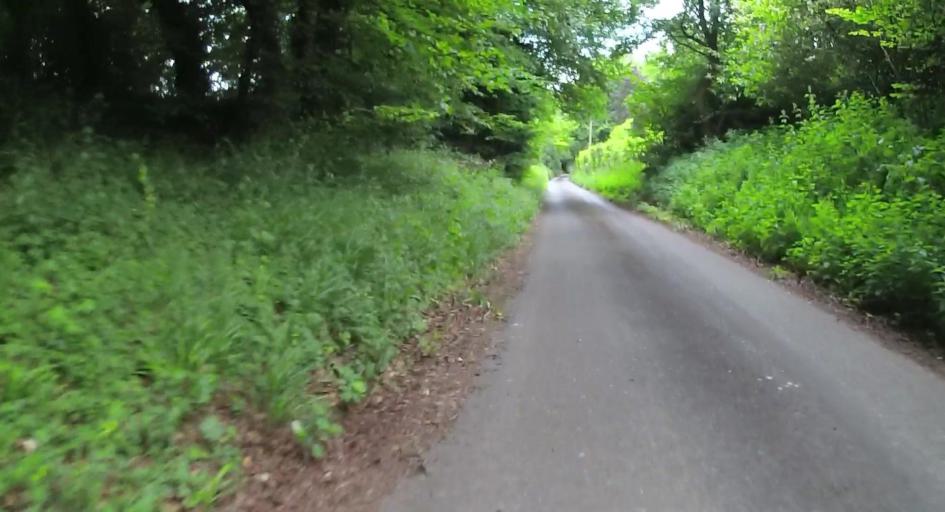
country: GB
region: England
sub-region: Hampshire
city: Four Marks
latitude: 51.1580
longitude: -1.1597
